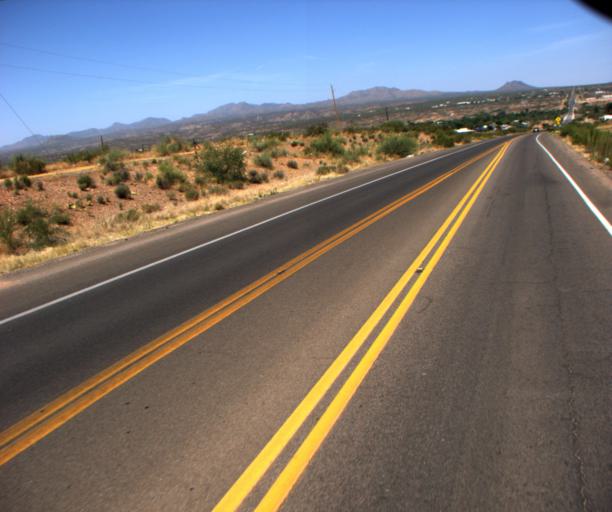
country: US
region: Arizona
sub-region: Gila County
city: Peridot
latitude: 33.2934
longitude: -110.4396
